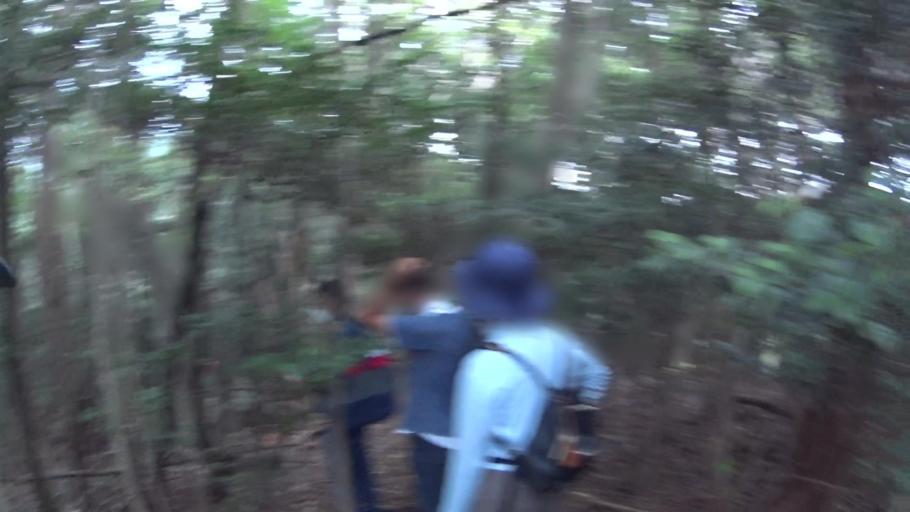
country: JP
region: Osaka
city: Kaizuka
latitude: 34.4736
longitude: 135.3061
